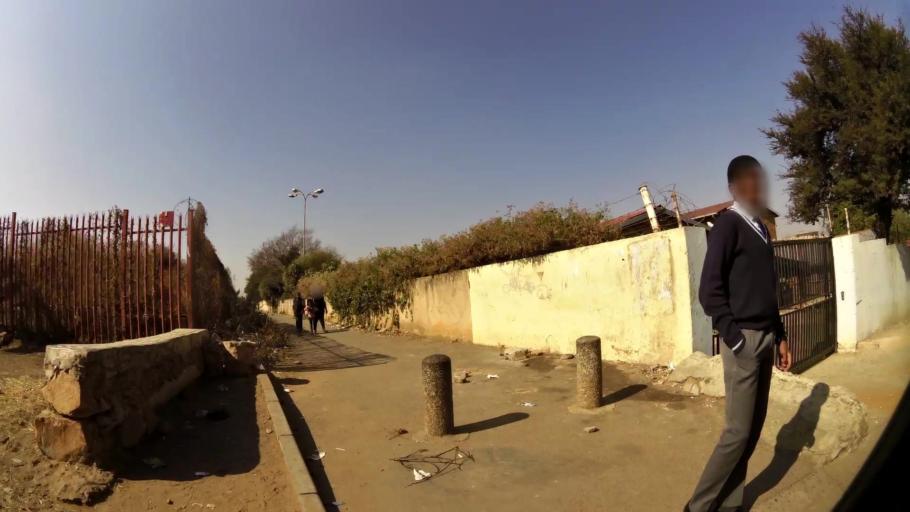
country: ZA
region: Gauteng
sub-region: City of Johannesburg Metropolitan Municipality
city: Soweto
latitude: -26.2519
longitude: 27.9418
